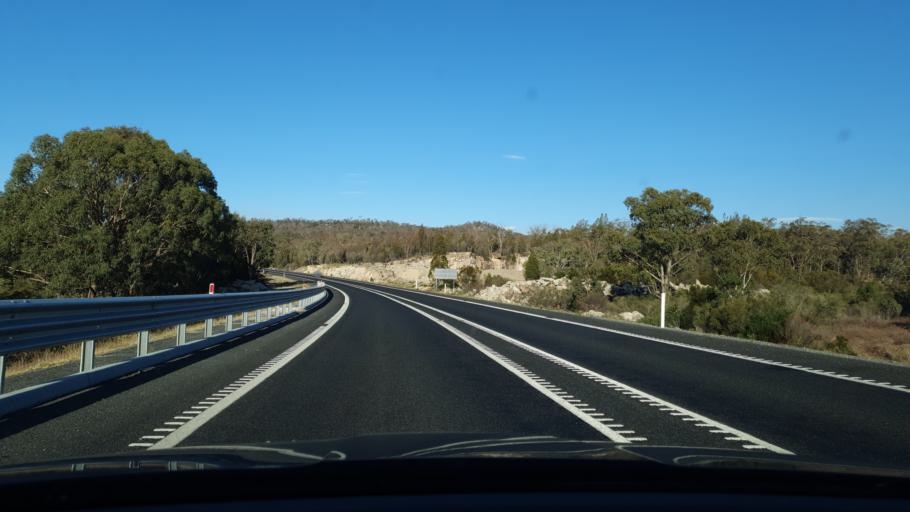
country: AU
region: Queensland
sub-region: Southern Downs
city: Stanthorpe
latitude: -28.6840
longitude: 151.9162
